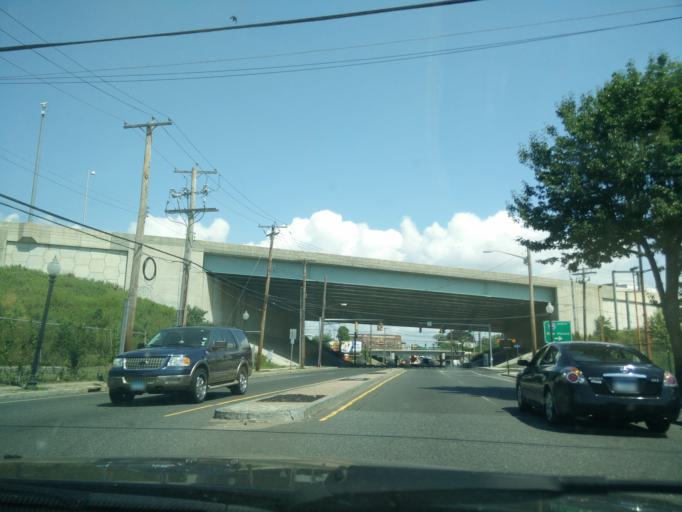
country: US
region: Connecticut
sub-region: Fairfield County
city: Bridgeport
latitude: 41.1660
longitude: -73.2180
